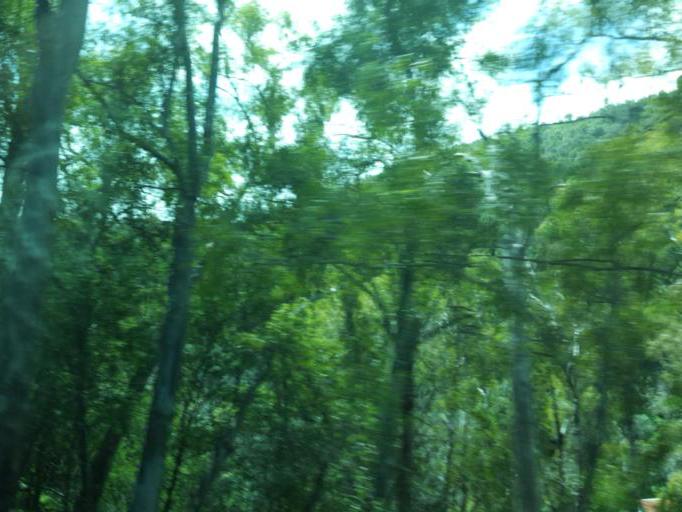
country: PT
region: Faro
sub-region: Monchique
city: Monchique
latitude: 37.2829
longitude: -8.5537
